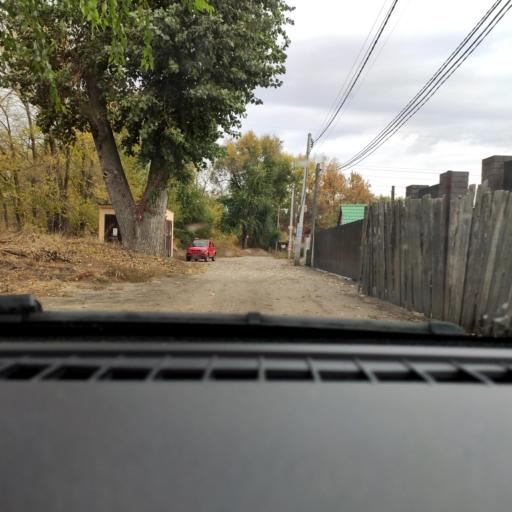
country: RU
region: Voronezj
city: Maslovka
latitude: 51.6021
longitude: 39.2315
